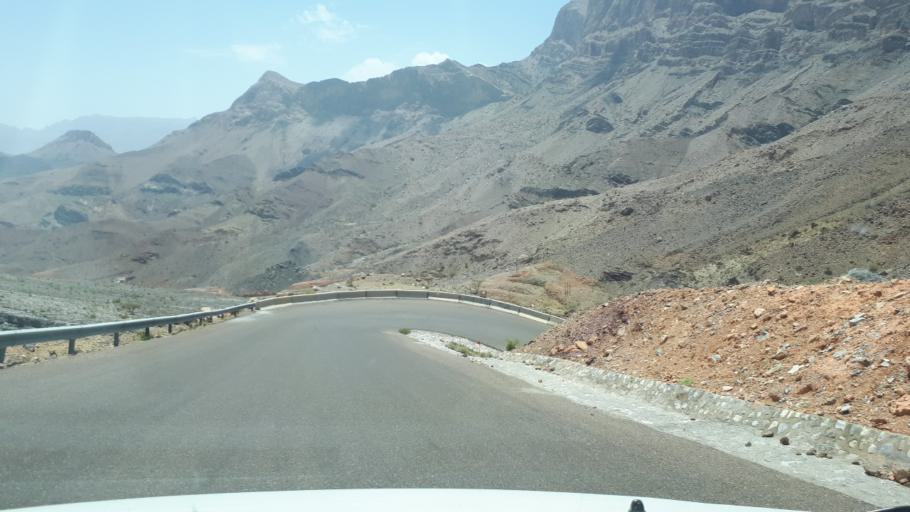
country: OM
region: Muhafazat ad Dakhiliyah
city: Bahla'
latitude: 23.2040
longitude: 57.1455
